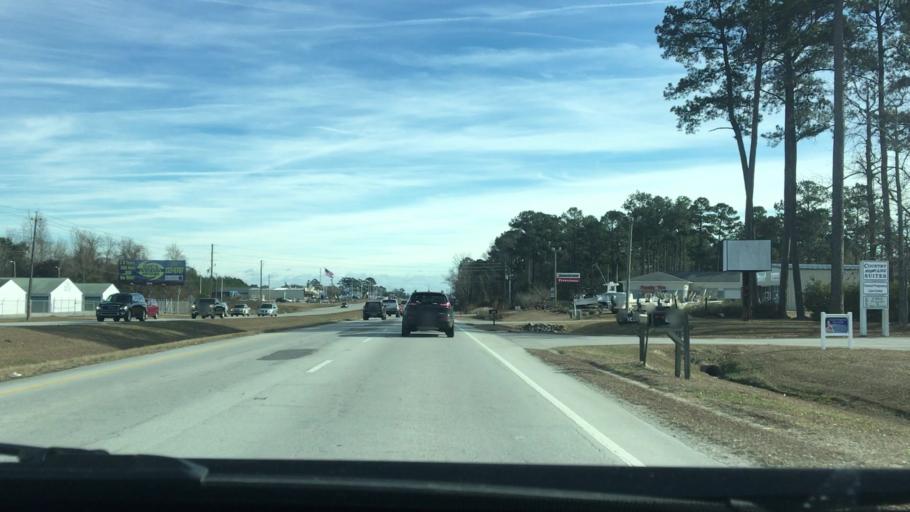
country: US
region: North Carolina
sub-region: Carteret County
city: Pine Knoll Shores
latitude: 34.7446
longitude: -76.8287
